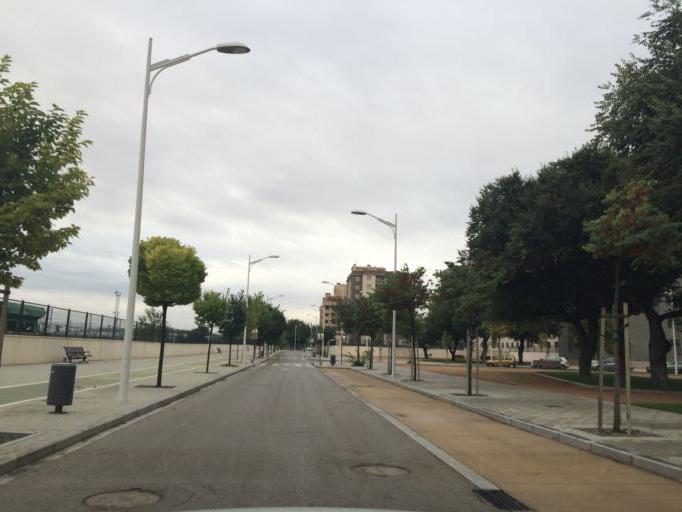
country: ES
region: Castille-La Mancha
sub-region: Provincia de Albacete
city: Albacete
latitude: 39.0088
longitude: -1.8581
